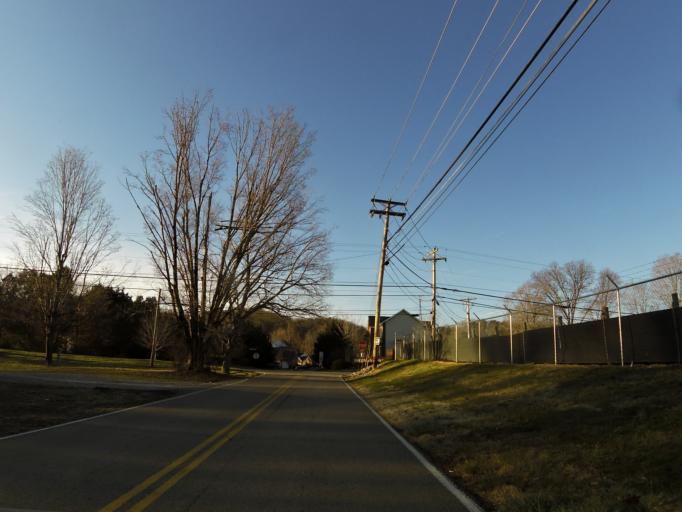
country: US
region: Tennessee
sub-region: Knox County
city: Farragut
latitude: 35.9470
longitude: -84.1275
